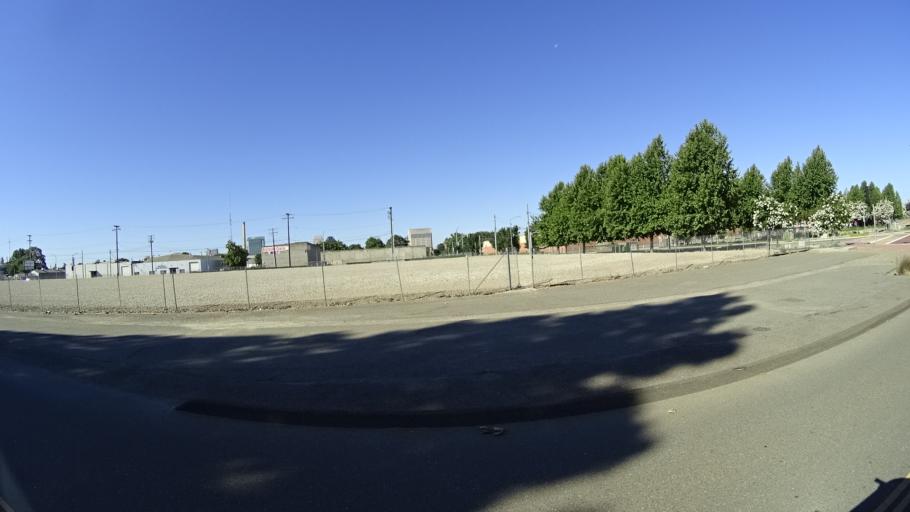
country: US
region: California
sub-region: Sacramento County
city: Sacramento
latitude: 38.5967
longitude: -121.4902
